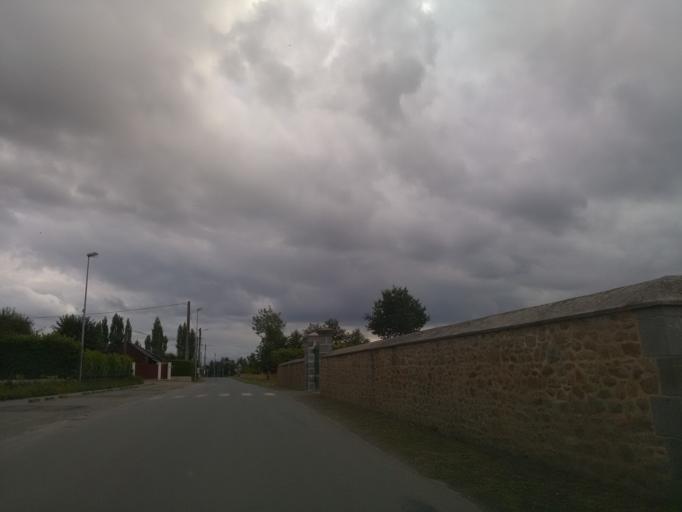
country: FR
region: Brittany
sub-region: Departement d'Ille-et-Vilaine
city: Vignoc
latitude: 48.2481
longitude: -1.7862
